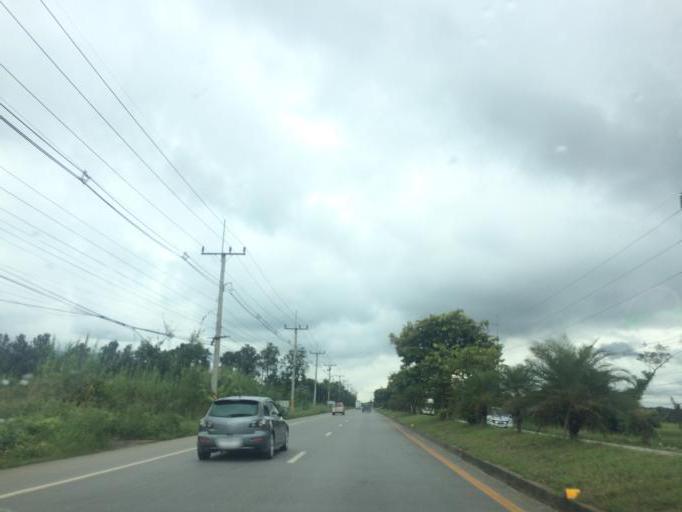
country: TH
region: Chiang Rai
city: Mae Chan
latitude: 20.0593
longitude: 99.8754
